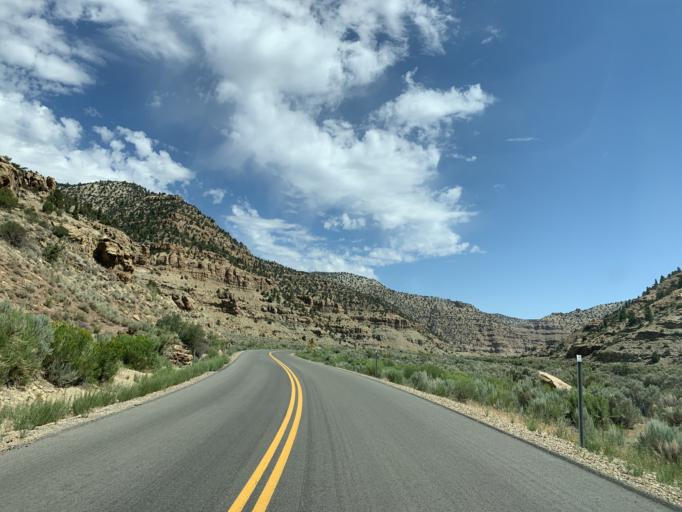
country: US
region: Utah
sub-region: Carbon County
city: East Carbon City
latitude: 39.7886
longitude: -110.3941
